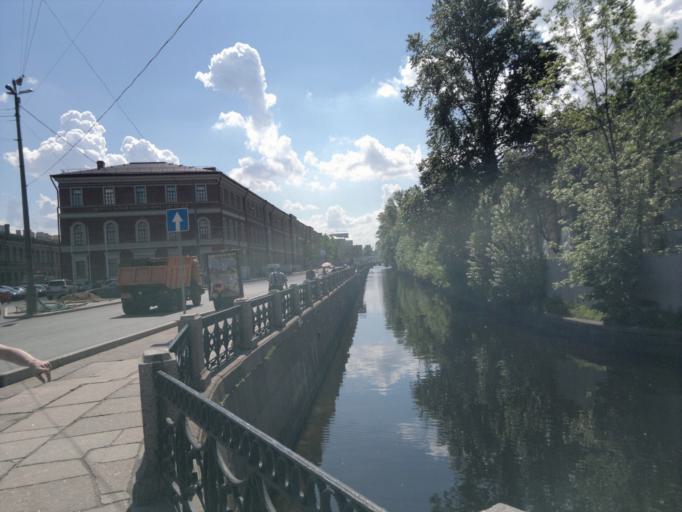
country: RU
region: St.-Petersburg
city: Saint Petersburg
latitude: 59.9314
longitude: 30.2920
